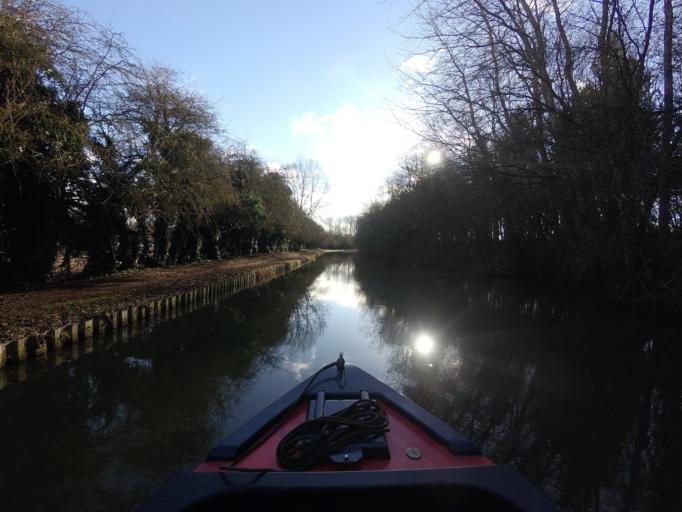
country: GB
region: England
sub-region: Northamptonshire
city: Long Buckby
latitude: 52.2621
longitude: -1.0894
